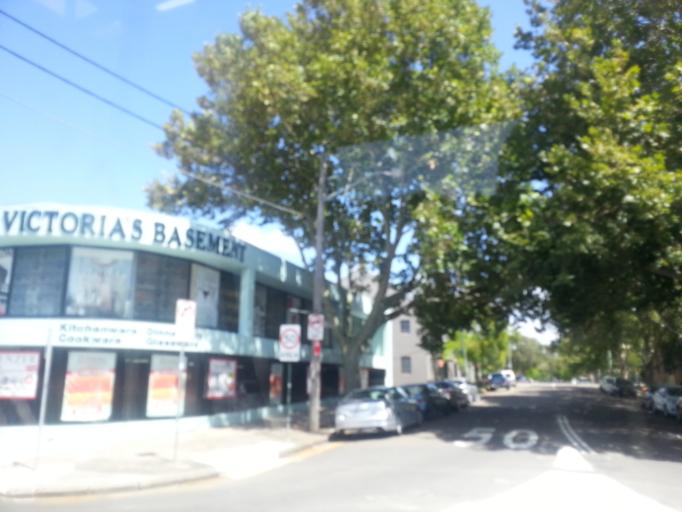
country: AU
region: New South Wales
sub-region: City of Sydney
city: Alexandria
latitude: -33.9042
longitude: 151.1935
